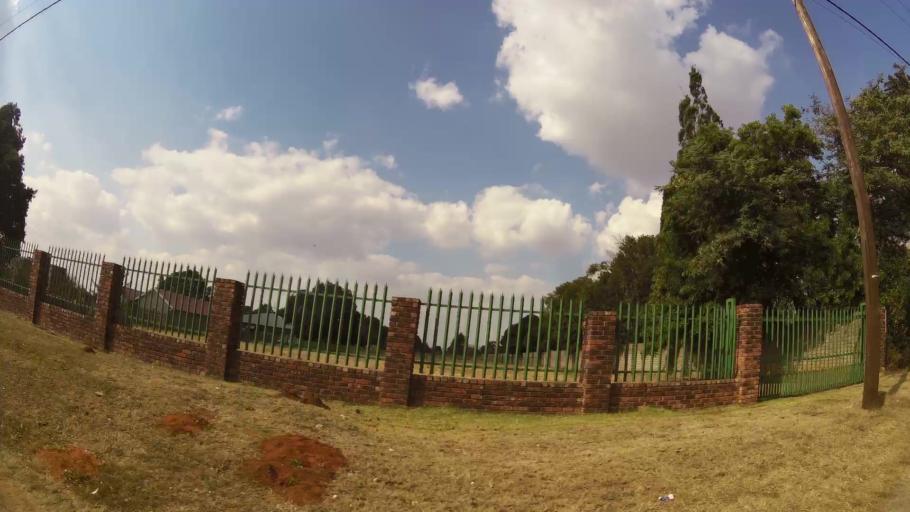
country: ZA
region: Mpumalanga
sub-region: Nkangala District Municipality
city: Delmas
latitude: -26.1489
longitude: 28.5492
